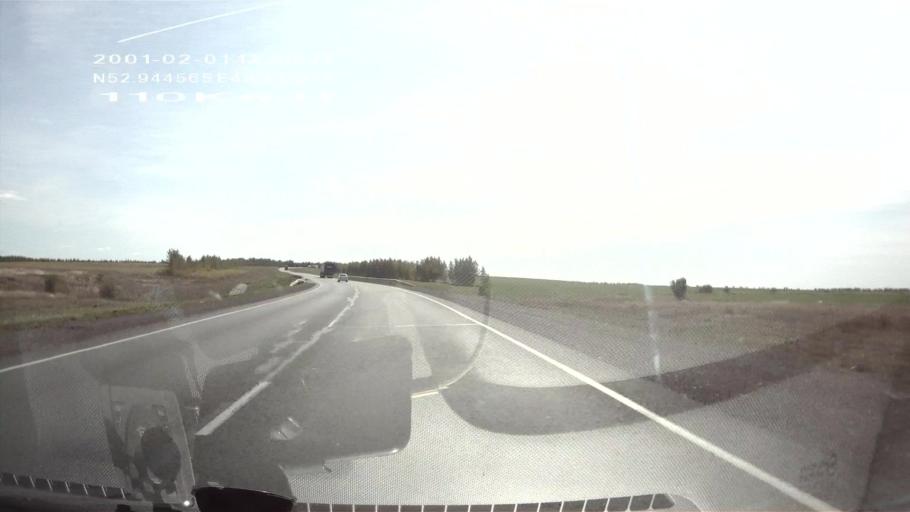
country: RU
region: Samara
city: Syzran'
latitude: 52.9430
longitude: 48.3042
